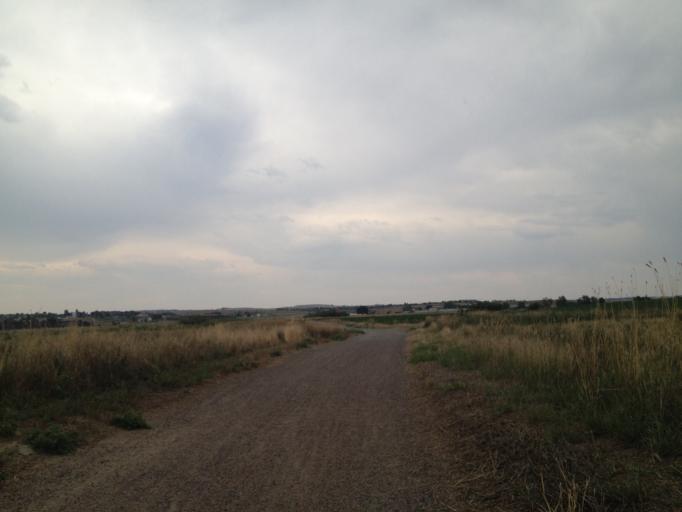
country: US
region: Colorado
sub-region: Boulder County
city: Erie
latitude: 40.0159
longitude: -105.0518
